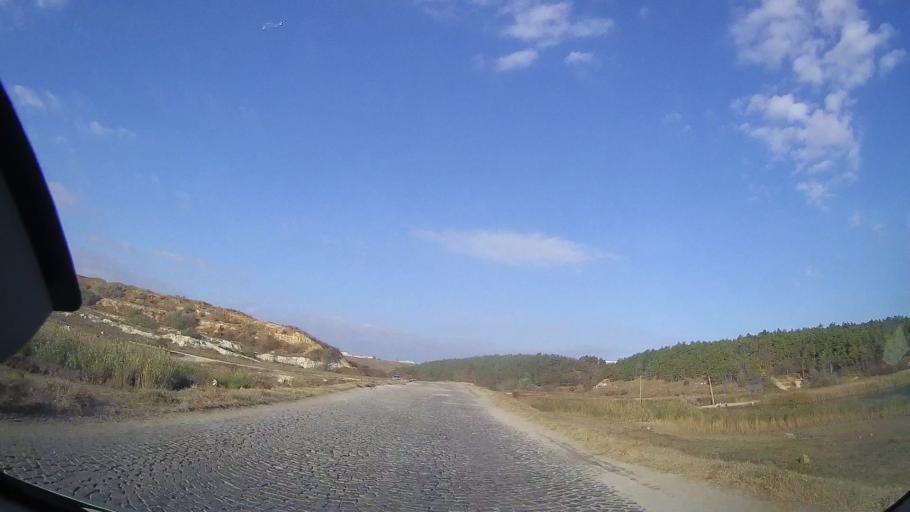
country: RO
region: Constanta
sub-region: Comuna Limanu
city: Limanu
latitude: 43.8133
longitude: 28.5169
